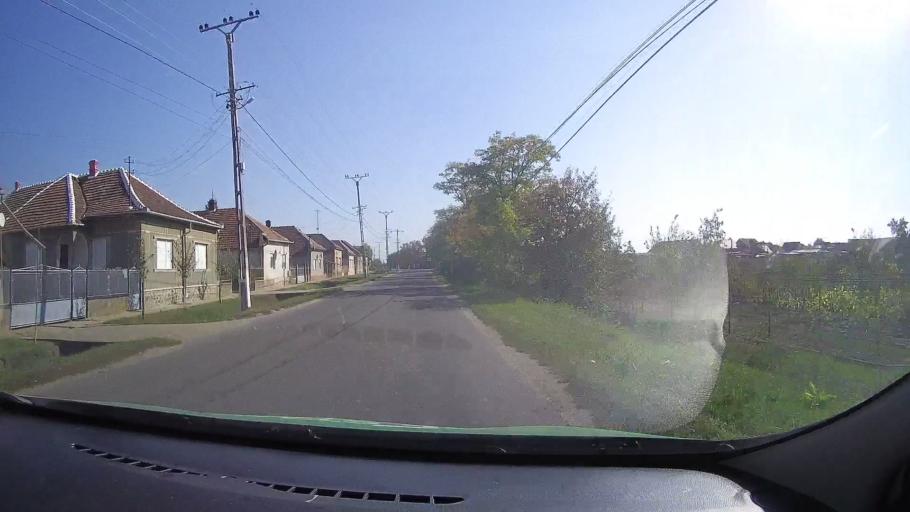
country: RO
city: Foieni
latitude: 47.6956
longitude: 22.3954
